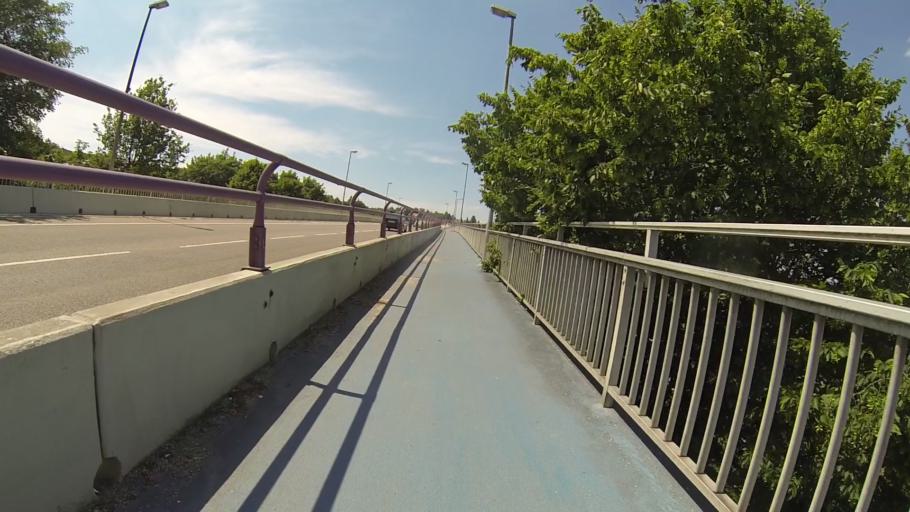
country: DE
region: Baden-Wuerttemberg
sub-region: Regierungsbezirk Stuttgart
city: Giengen an der Brenz
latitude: 48.6214
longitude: 10.2366
